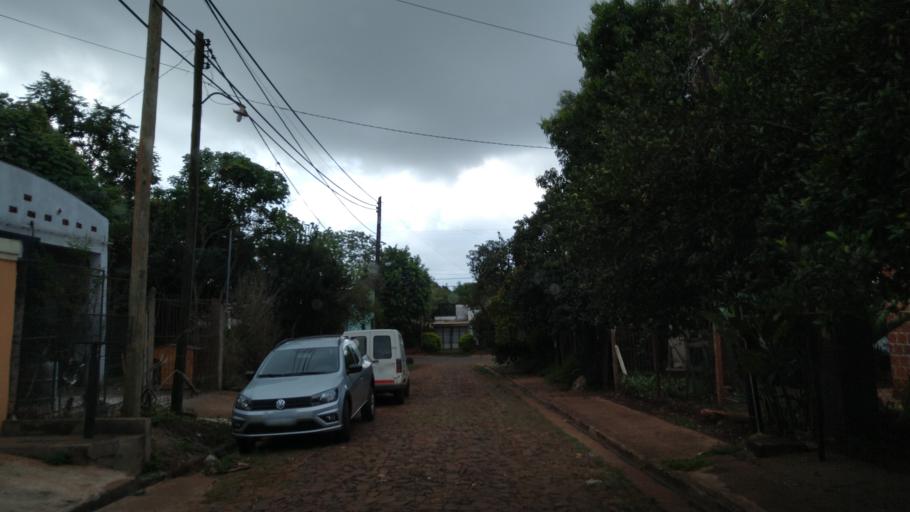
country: AR
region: Misiones
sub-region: Departamento de Capital
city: Posadas
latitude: -27.4110
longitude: -55.9038
